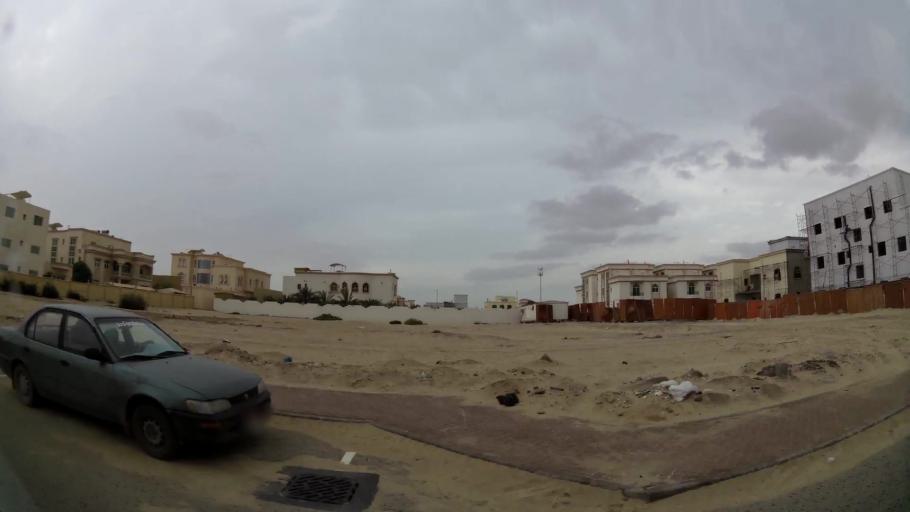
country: AE
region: Abu Dhabi
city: Abu Dhabi
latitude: 24.3691
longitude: 54.6483
